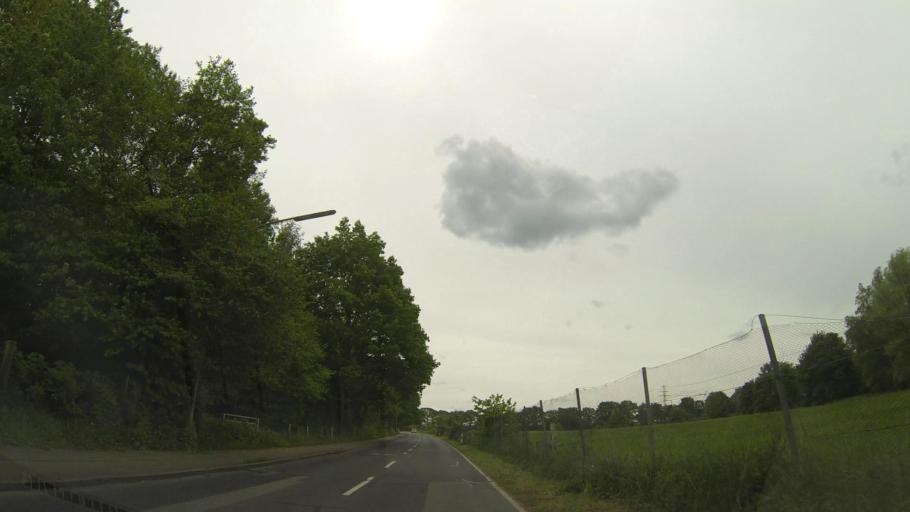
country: DE
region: Schleswig-Holstein
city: Ellerbek
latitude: 53.6395
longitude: 9.8711
